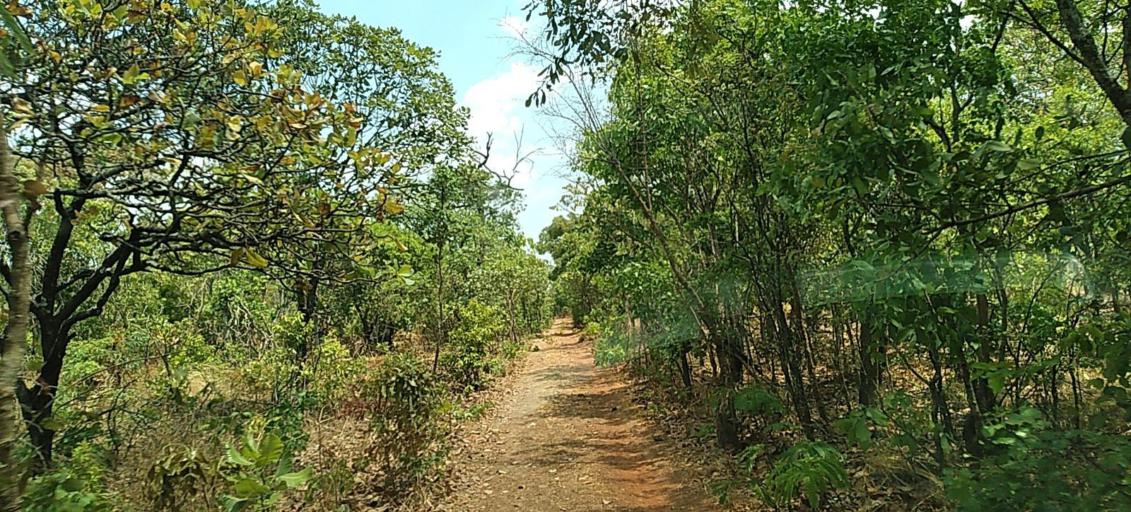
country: CD
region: Katanga
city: Kipushi
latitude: -11.9817
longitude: 27.4157
